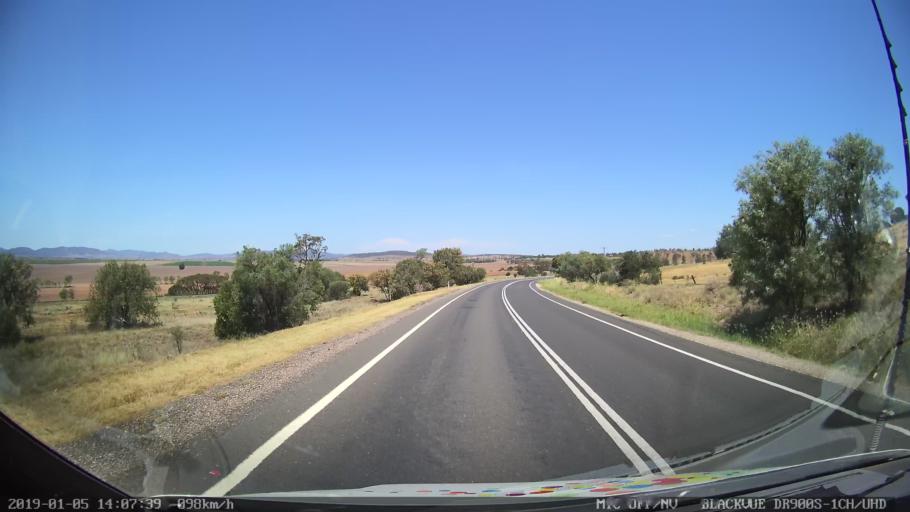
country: AU
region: New South Wales
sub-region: Gunnedah
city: Gunnedah
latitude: -31.2245
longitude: 150.4092
